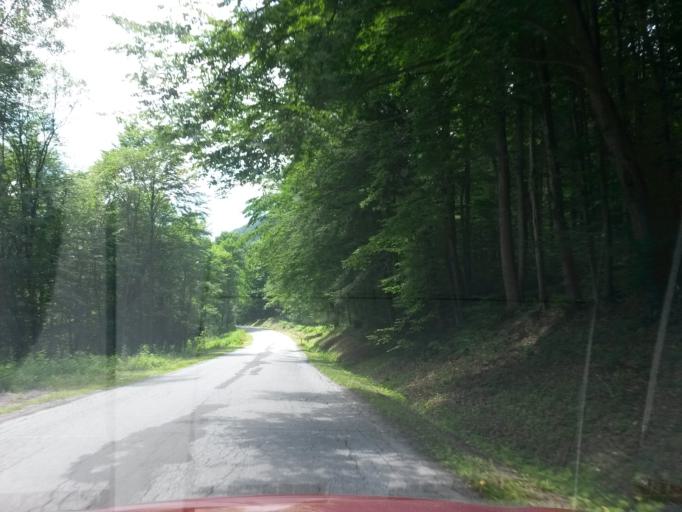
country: SK
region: Kosicky
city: Gelnica
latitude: 48.9203
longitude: 21.0379
